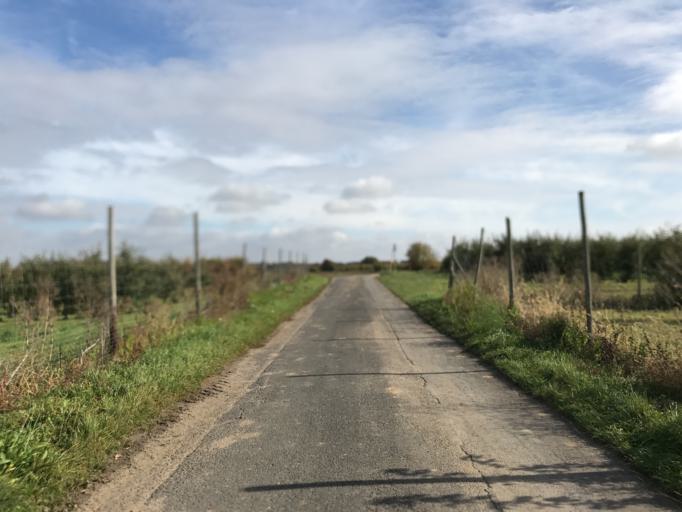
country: DE
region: Rheinland-Pfalz
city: Wackernheim
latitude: 49.9716
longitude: 8.1041
